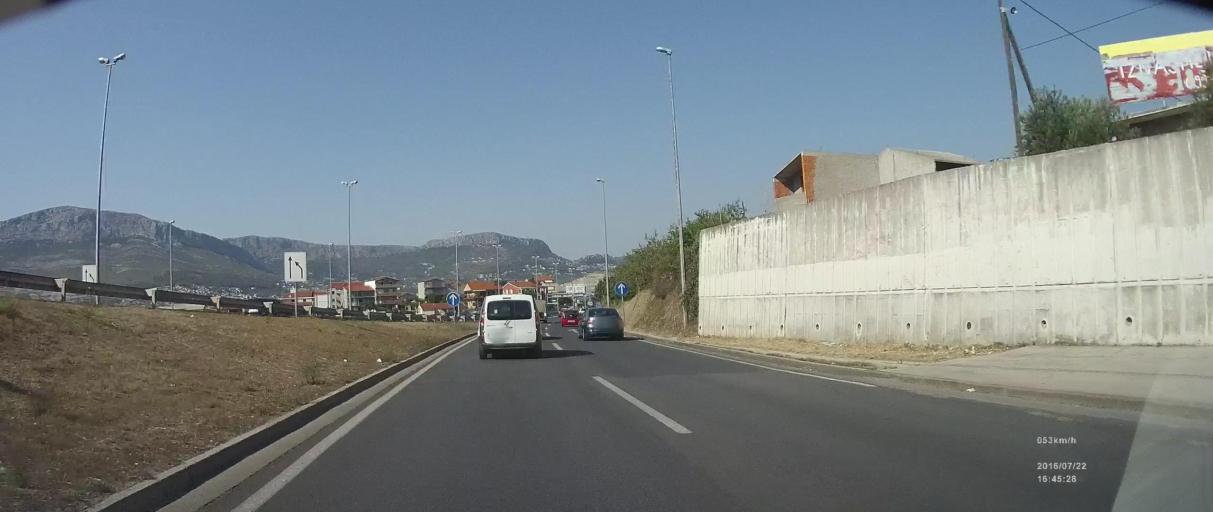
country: HR
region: Splitsko-Dalmatinska
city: Vranjic
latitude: 43.5194
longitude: 16.4818
